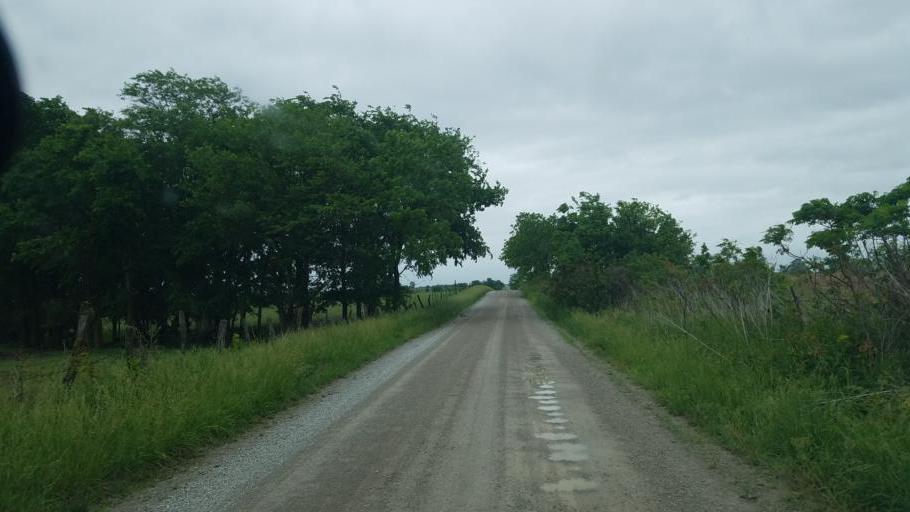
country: US
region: Missouri
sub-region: Carroll County
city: Carrollton
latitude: 39.4852
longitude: -93.4889
